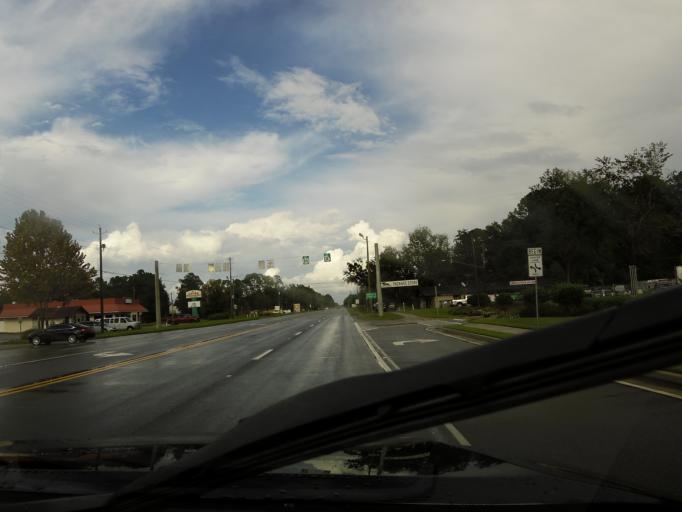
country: US
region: Georgia
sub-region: Liberty County
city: Walthourville
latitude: 31.7735
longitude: -81.6332
